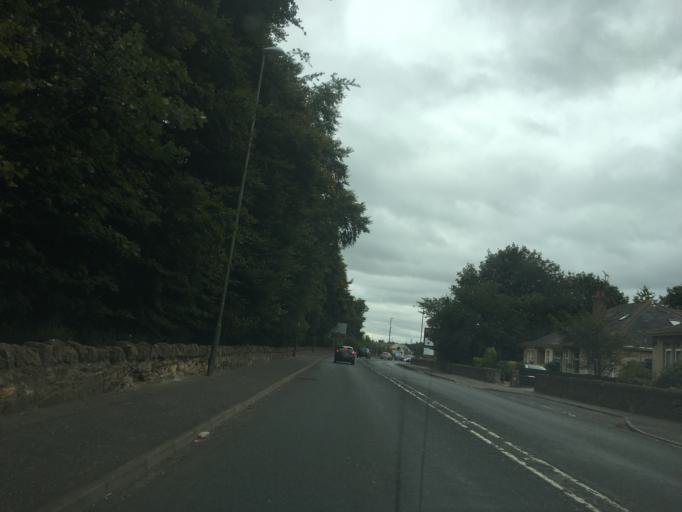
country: GB
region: Scotland
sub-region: Midlothian
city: Bonnyrigg
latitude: 55.8970
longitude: -3.1027
